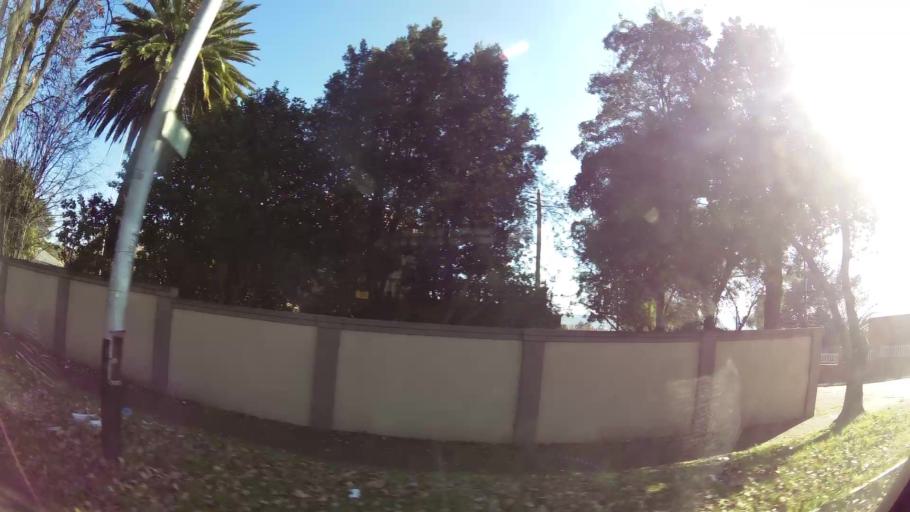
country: ZA
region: Gauteng
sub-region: City of Johannesburg Metropolitan Municipality
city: Johannesburg
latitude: -26.1922
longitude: 28.1019
